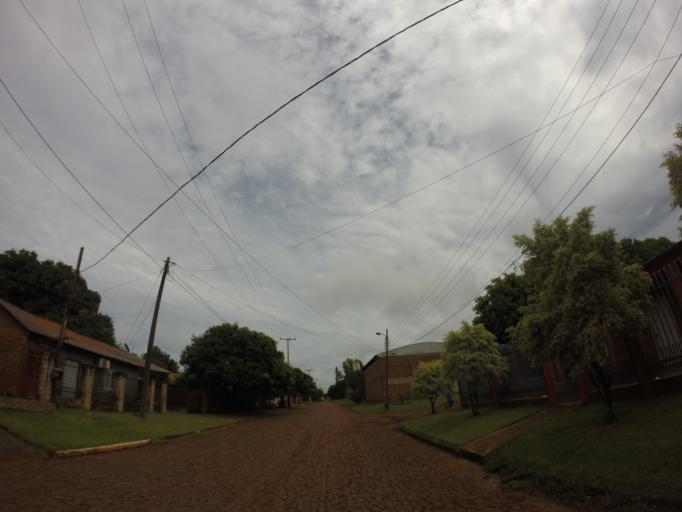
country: PY
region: Alto Parana
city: Ciudad del Este
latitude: -25.3882
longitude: -54.6500
